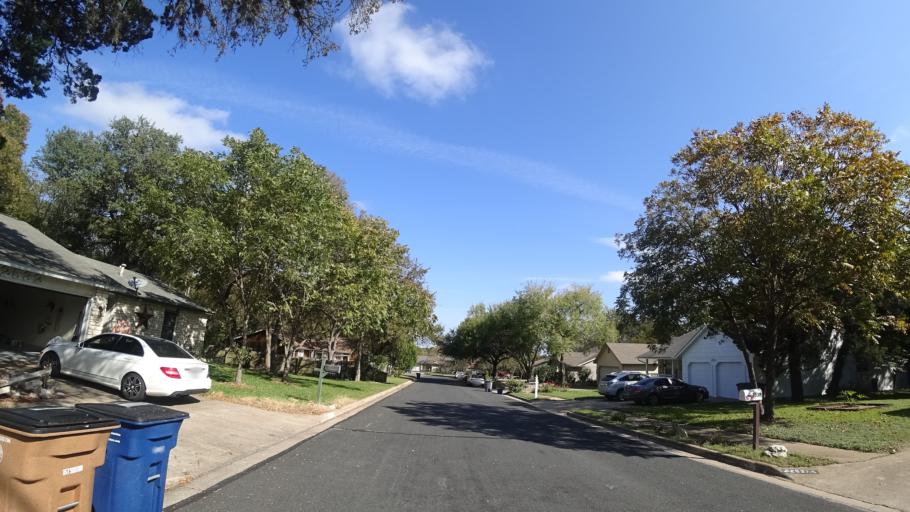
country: US
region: Texas
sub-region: Travis County
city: Shady Hollow
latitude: 30.1898
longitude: -97.8239
